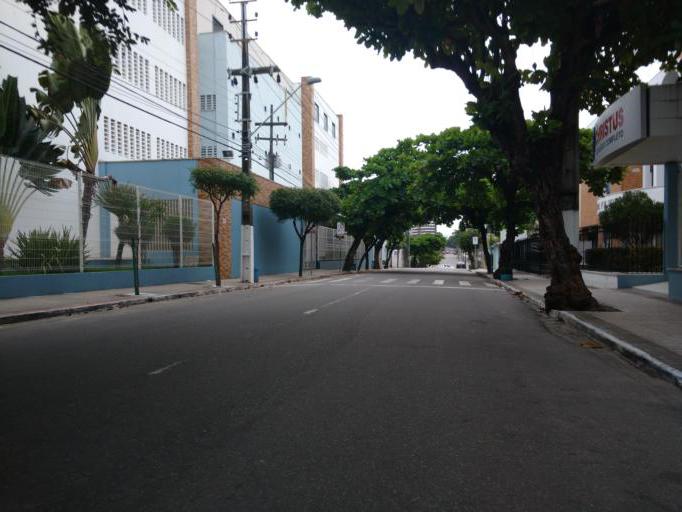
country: BR
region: Ceara
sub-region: Fortaleza
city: Fortaleza
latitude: -3.7382
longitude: -38.5066
